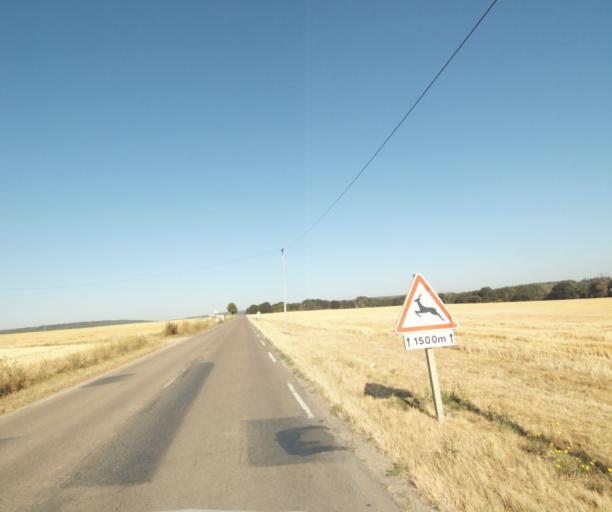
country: FR
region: Ile-de-France
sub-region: Departement de l'Essonne
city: Itteville
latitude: 48.5135
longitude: 2.3248
